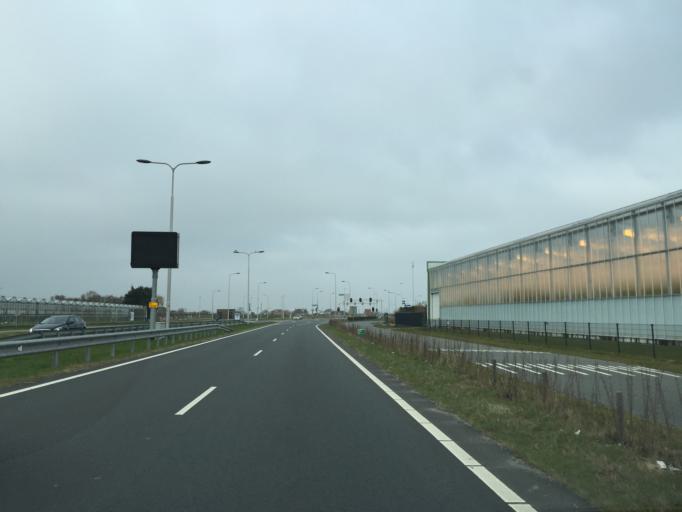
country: NL
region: South Holland
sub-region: Gemeente Rotterdam
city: Hoek van Holland
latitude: 51.9922
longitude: 4.1387
